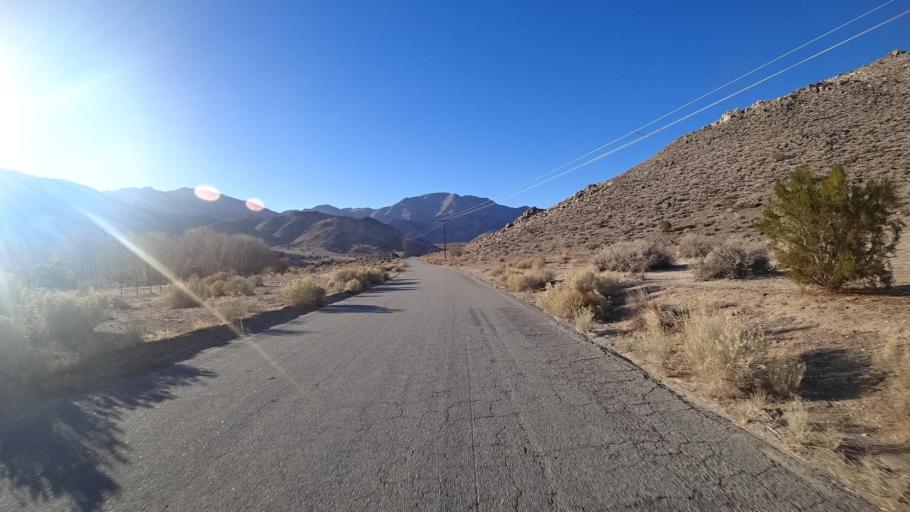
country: US
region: California
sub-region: Kern County
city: Weldon
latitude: 35.5650
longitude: -118.2440
